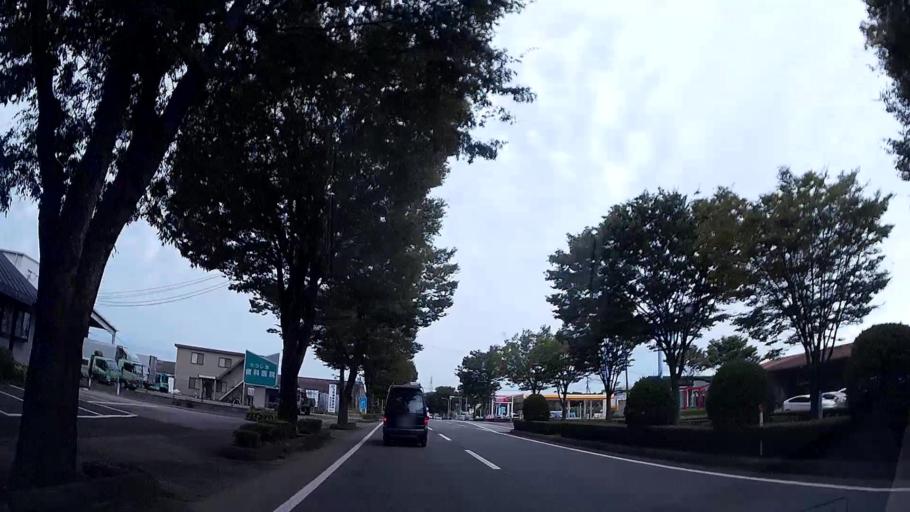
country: JP
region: Kumamoto
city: Ozu
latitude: 32.8971
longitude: 130.8535
